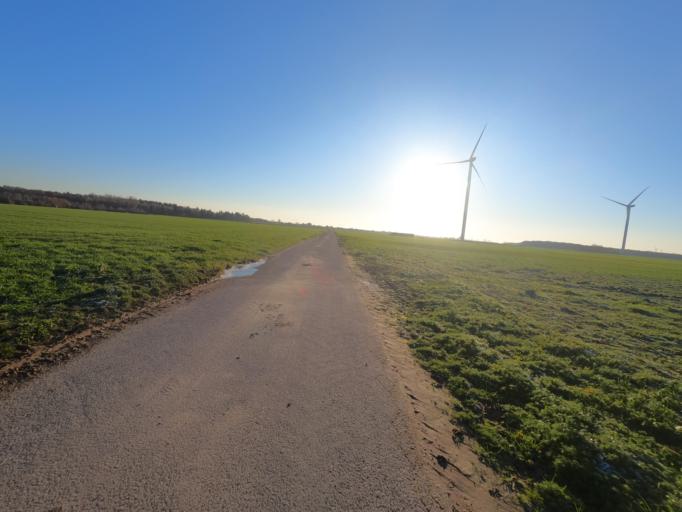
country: DE
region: North Rhine-Westphalia
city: Geilenkirchen
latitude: 51.0027
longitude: 6.1029
